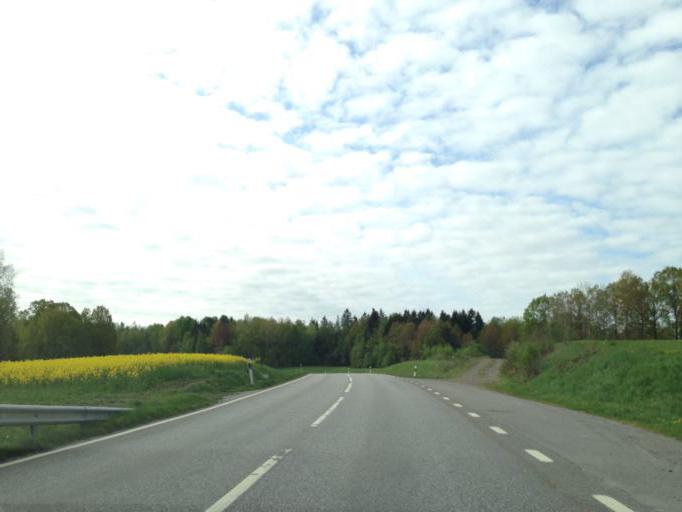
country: SE
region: Soedermanland
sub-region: Flens Kommun
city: Malmkoping
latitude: 59.0816
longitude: 16.8082
